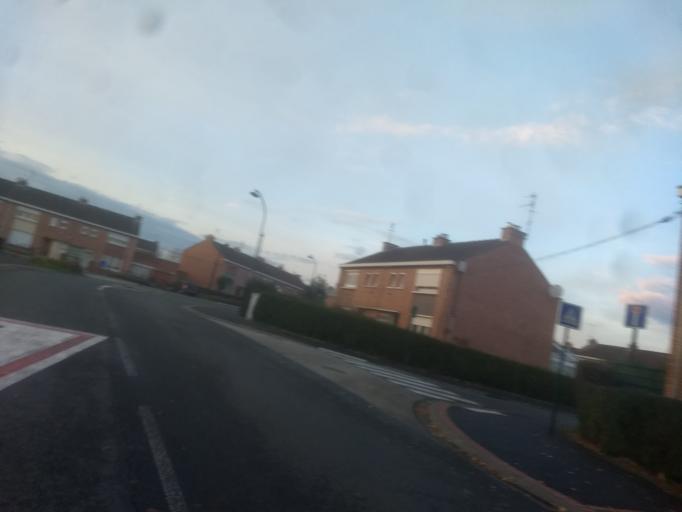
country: FR
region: Nord-Pas-de-Calais
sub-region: Departement du Pas-de-Calais
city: Dainville
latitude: 50.2872
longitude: 2.7377
